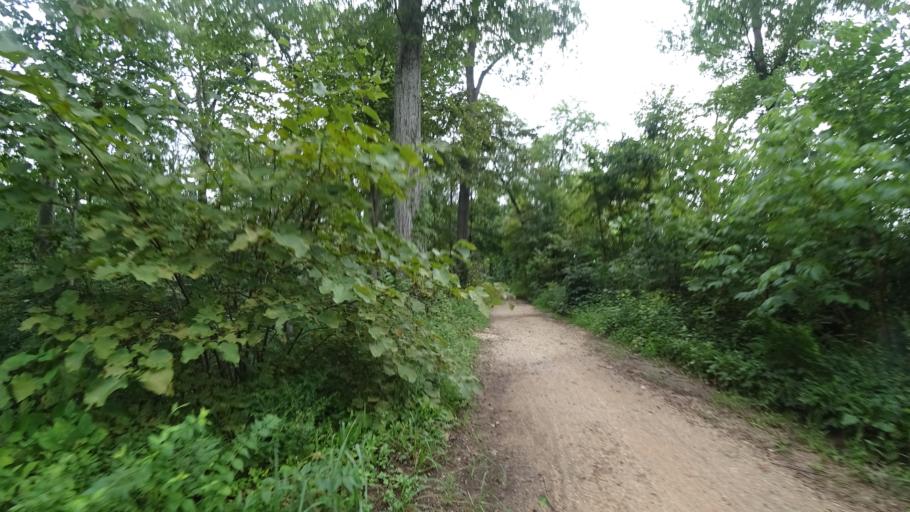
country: US
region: Virginia
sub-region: Loudoun County
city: Lowes Island
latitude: 39.0672
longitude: -77.3764
